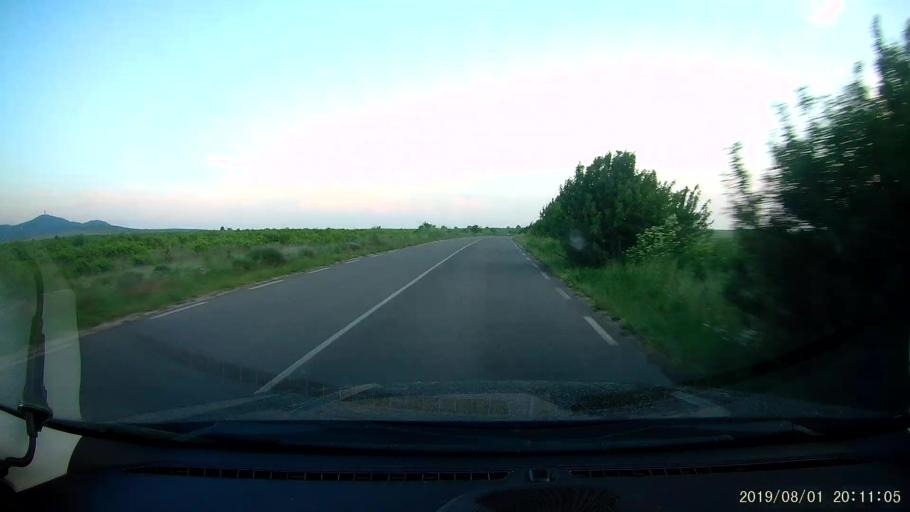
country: BG
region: Yambol
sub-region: Obshtina Yambol
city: Yambol
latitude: 42.4684
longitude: 26.6051
